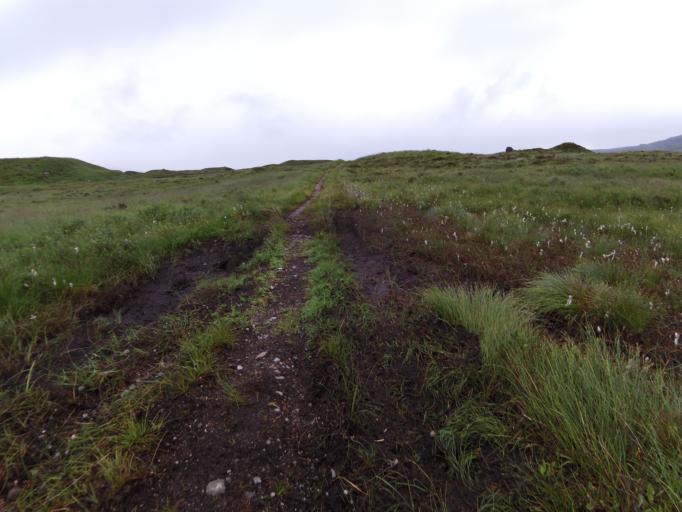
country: GB
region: Scotland
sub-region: Highland
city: Spean Bridge
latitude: 56.7682
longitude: -4.7043
